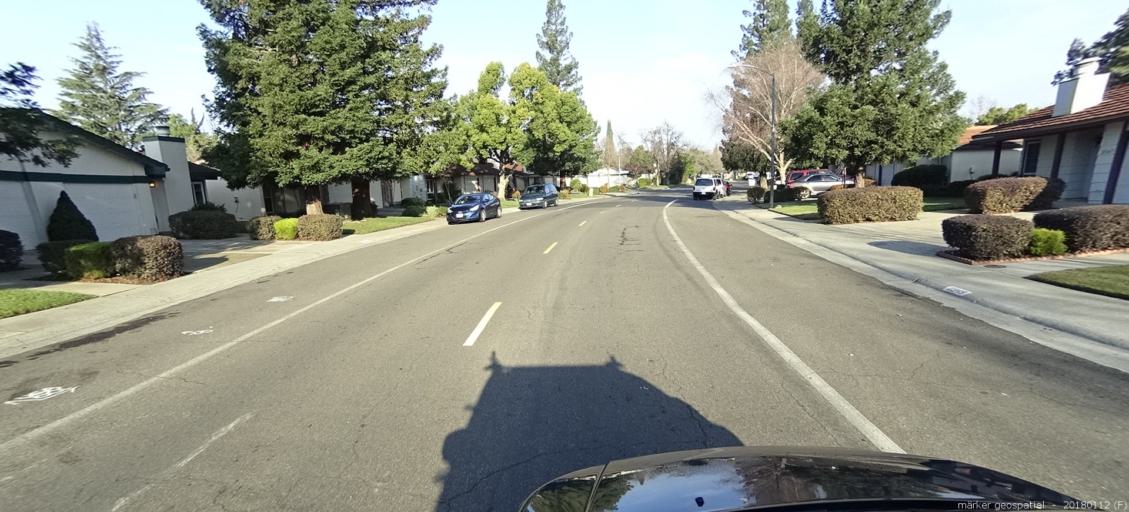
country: US
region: California
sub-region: Sacramento County
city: Gold River
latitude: 38.6117
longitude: -121.2752
